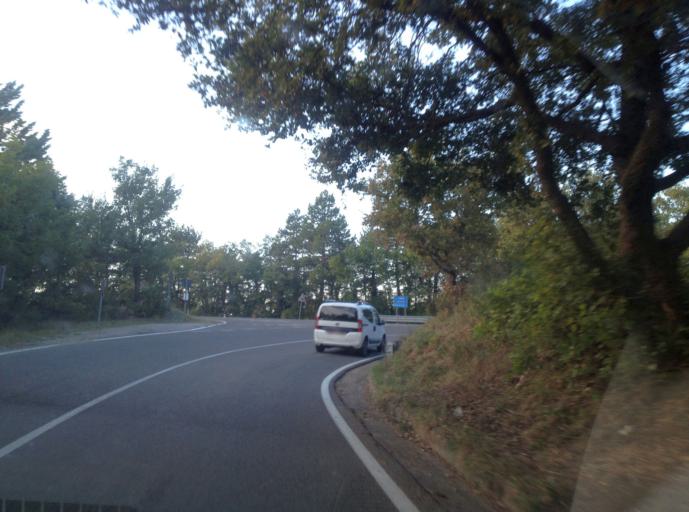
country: IT
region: Tuscany
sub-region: Provincia di Siena
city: Castellina in Chianti
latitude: 43.4263
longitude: 11.3056
